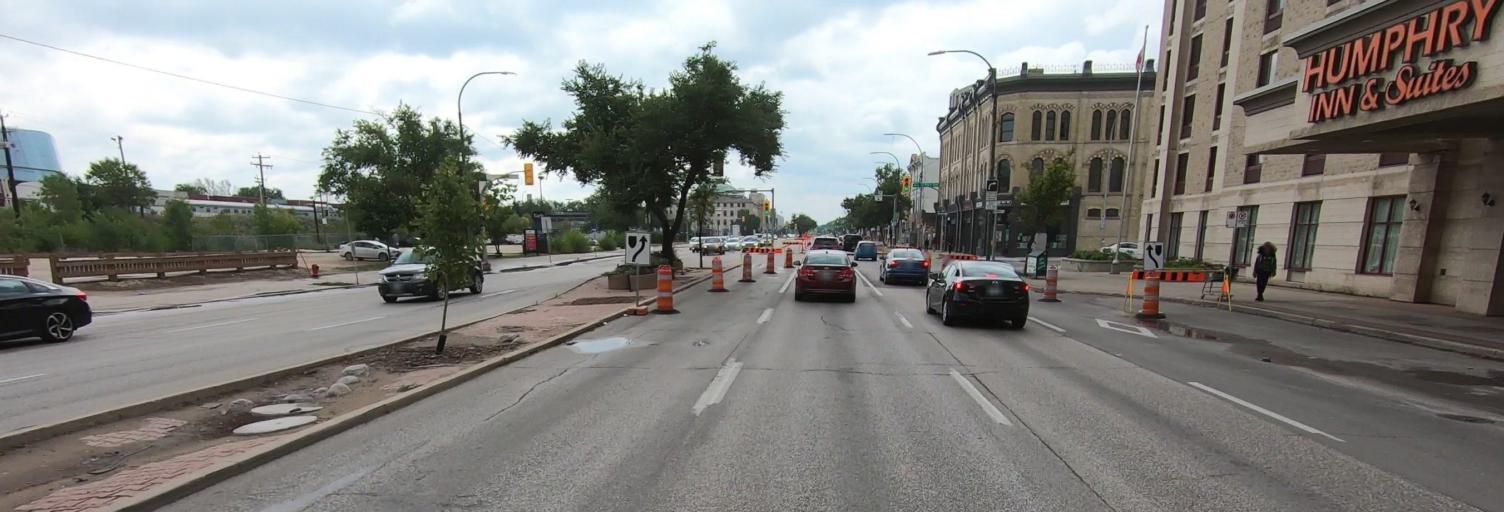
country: CA
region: Manitoba
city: Winnipeg
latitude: 49.8924
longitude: -97.1369
